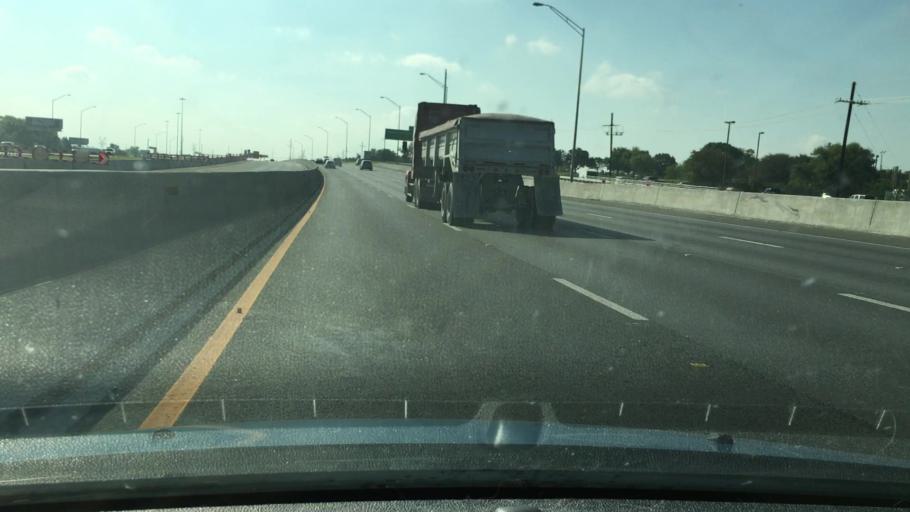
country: US
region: Texas
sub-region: Denton County
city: Highland Village
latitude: 33.0792
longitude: -97.0253
